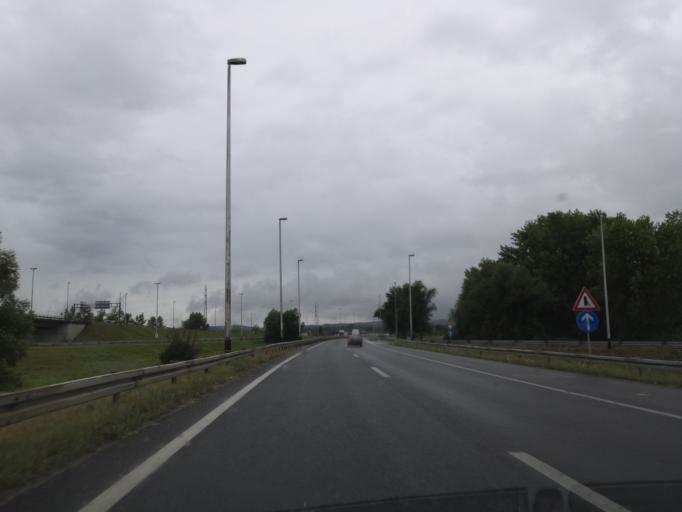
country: HR
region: Grad Zagreb
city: Jezdovec
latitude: 45.7882
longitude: 15.8466
